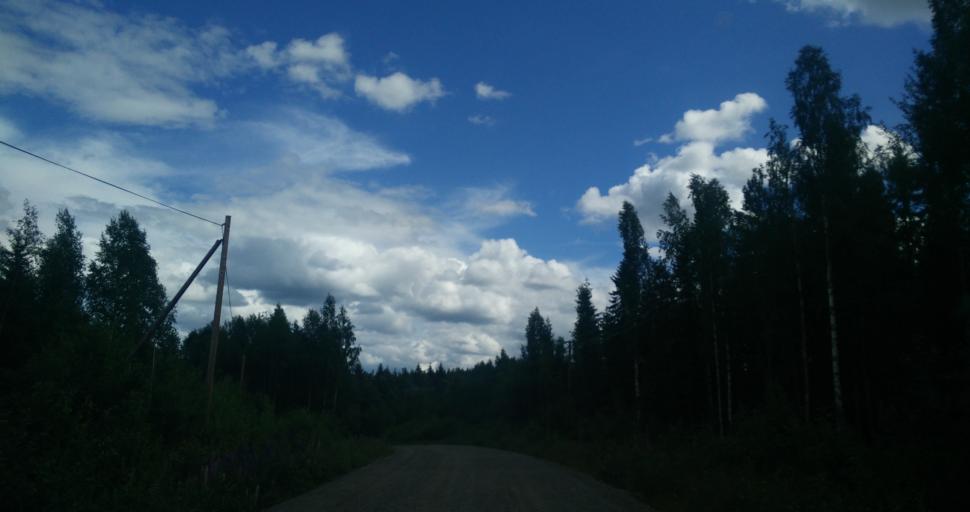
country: SE
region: Gaevleborg
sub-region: Nordanstigs Kommun
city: Bergsjoe
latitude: 62.0557
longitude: 16.8181
